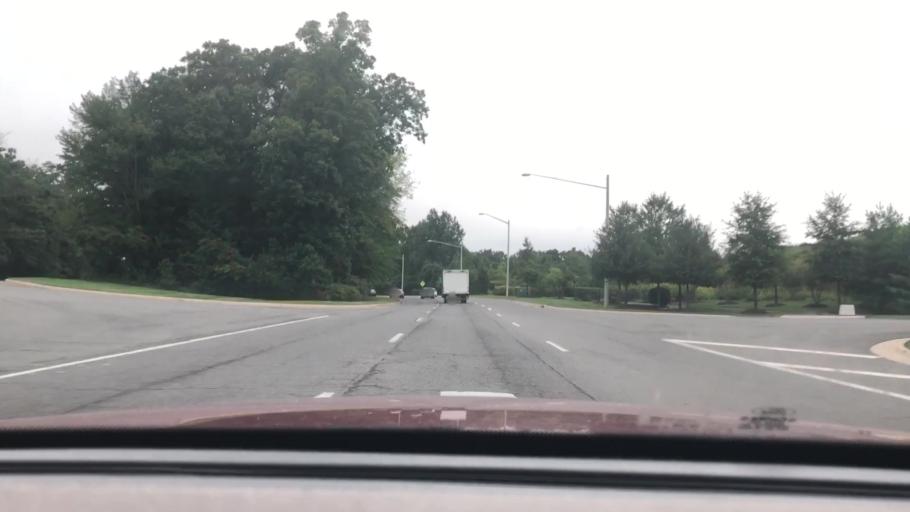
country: US
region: Virginia
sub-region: Fairfax County
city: Chantilly
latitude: 38.8739
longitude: -77.4540
